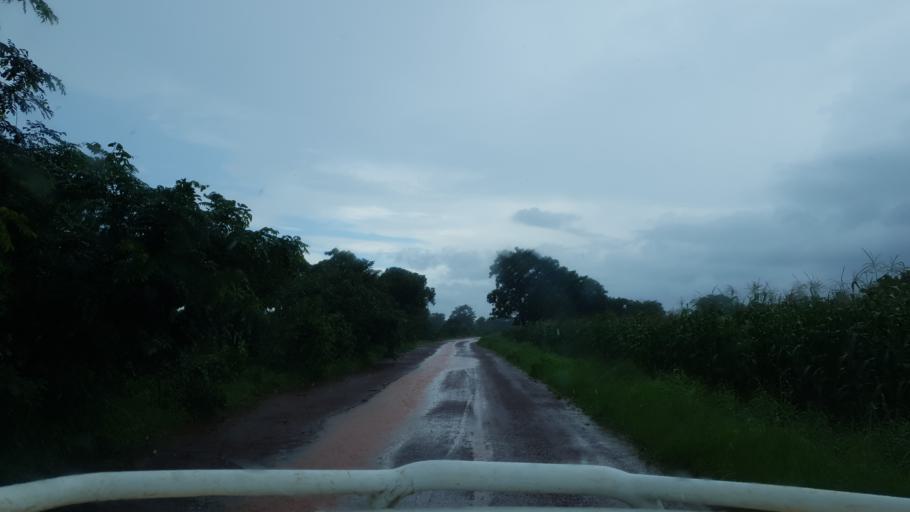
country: ML
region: Sikasso
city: Kolondieba
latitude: 11.5978
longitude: -6.6664
